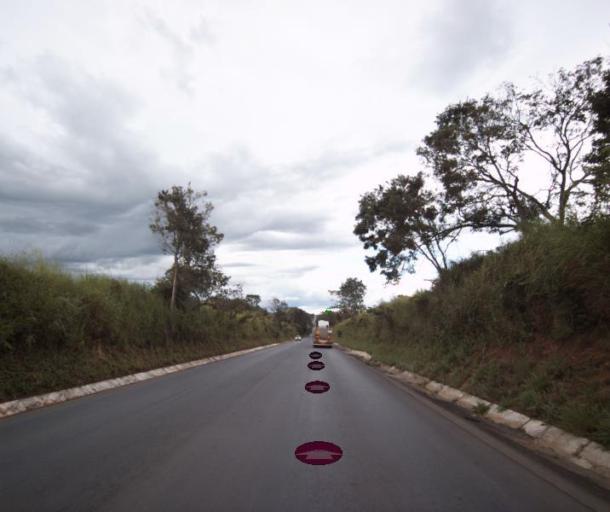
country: BR
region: Goias
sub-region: Itapaci
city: Itapaci
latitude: -15.0072
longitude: -49.4157
